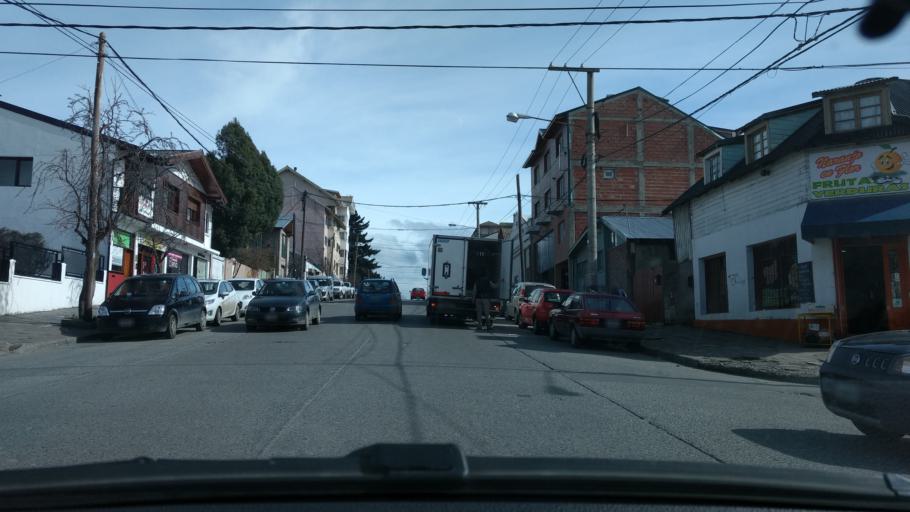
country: AR
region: Rio Negro
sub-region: Departamento de Bariloche
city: San Carlos de Bariloche
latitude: -41.1379
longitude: -71.2989
